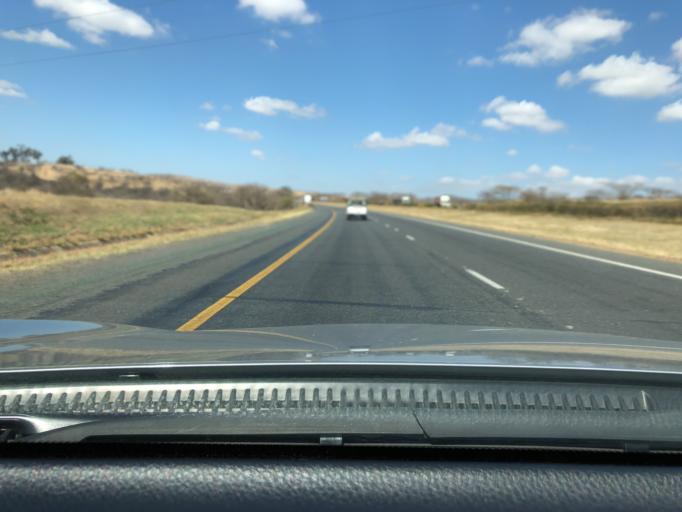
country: ZA
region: KwaZulu-Natal
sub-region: uThukela District Municipality
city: Estcourt
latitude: -28.9702
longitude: 29.7937
